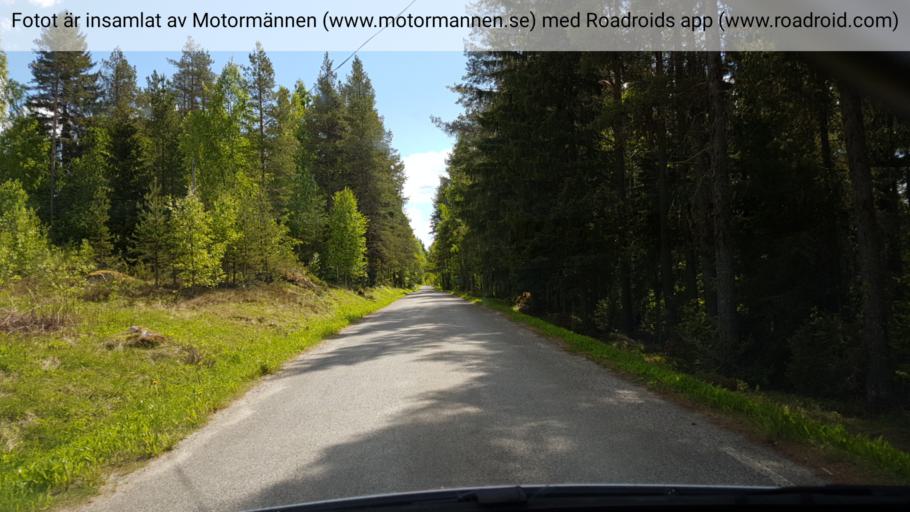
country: SE
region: Jaemtland
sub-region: OEstersunds Kommun
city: Brunflo
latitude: 63.0132
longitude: 15.1000
